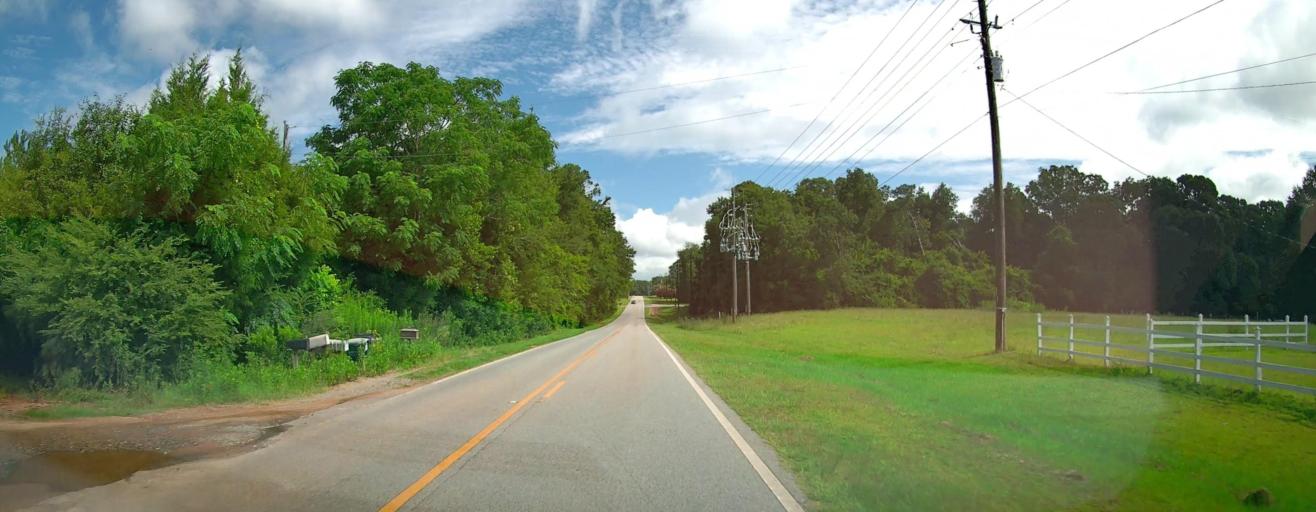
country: US
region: Georgia
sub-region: Peach County
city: Byron
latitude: 32.6297
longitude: -83.7997
